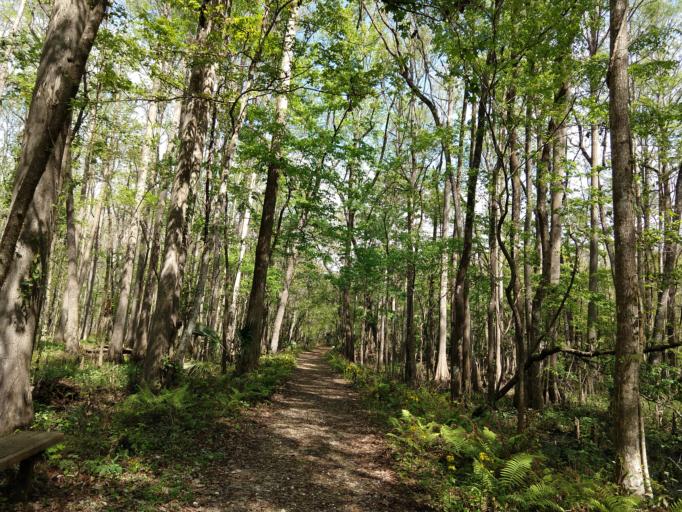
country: US
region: Florida
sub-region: Levy County
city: Manatee Road
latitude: 29.3774
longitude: -83.0442
